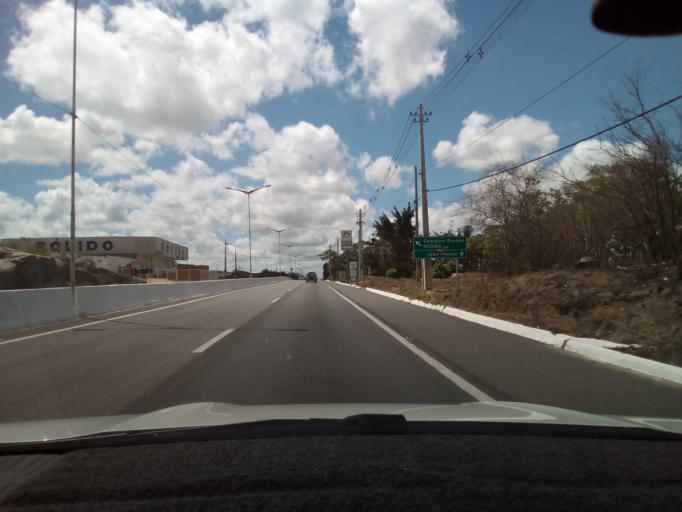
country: BR
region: Paraiba
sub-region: Campina Grande
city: Campina Grande
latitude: -7.2446
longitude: -35.8529
